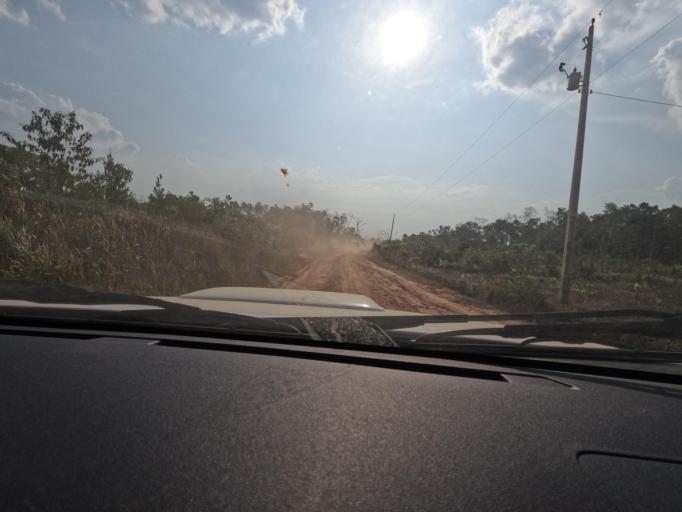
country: BR
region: Rondonia
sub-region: Porto Velho
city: Porto Velho
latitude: -8.5734
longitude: -64.0124
